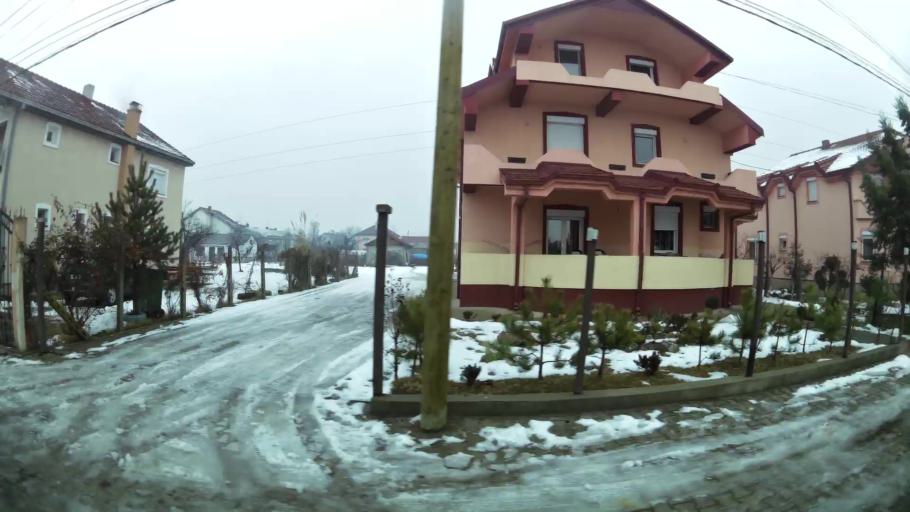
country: MK
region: Petrovec
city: Petrovec
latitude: 41.9353
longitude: 21.6117
